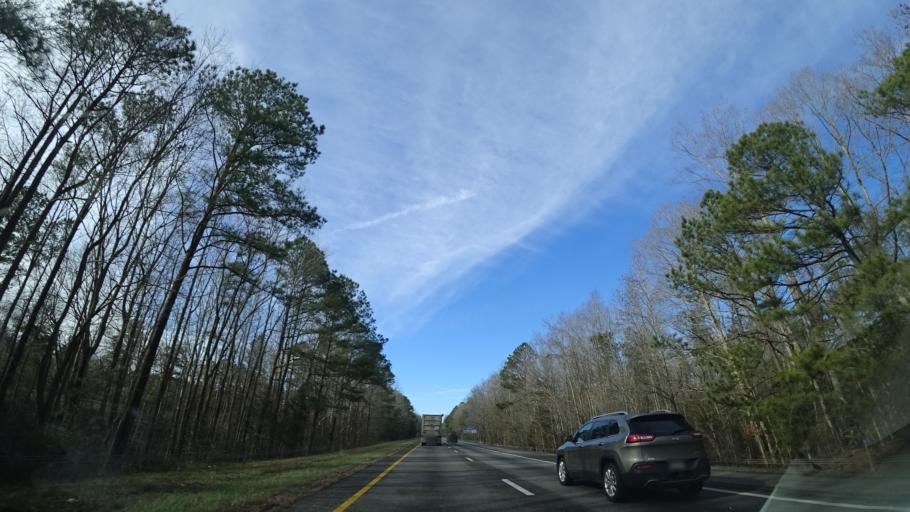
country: US
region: Virginia
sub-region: New Kent County
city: New Kent
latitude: 37.5009
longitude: -77.0711
